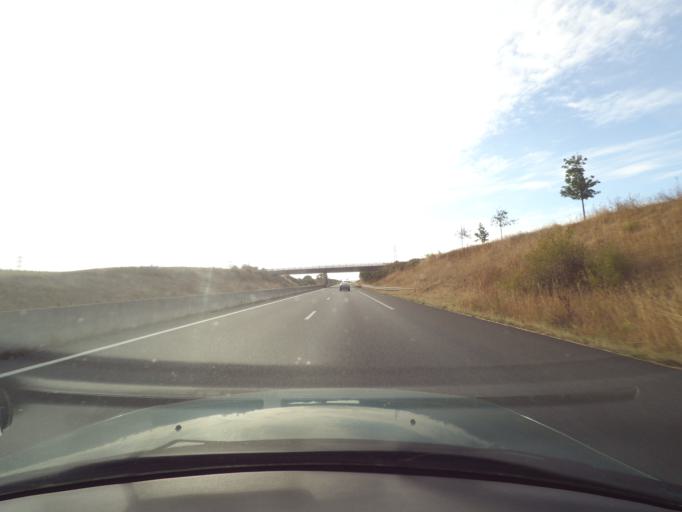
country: FR
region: Poitou-Charentes
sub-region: Departement des Deux-Sevres
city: Saint-Pierre-des-Echaubrognes
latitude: 46.9302
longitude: -0.7292
